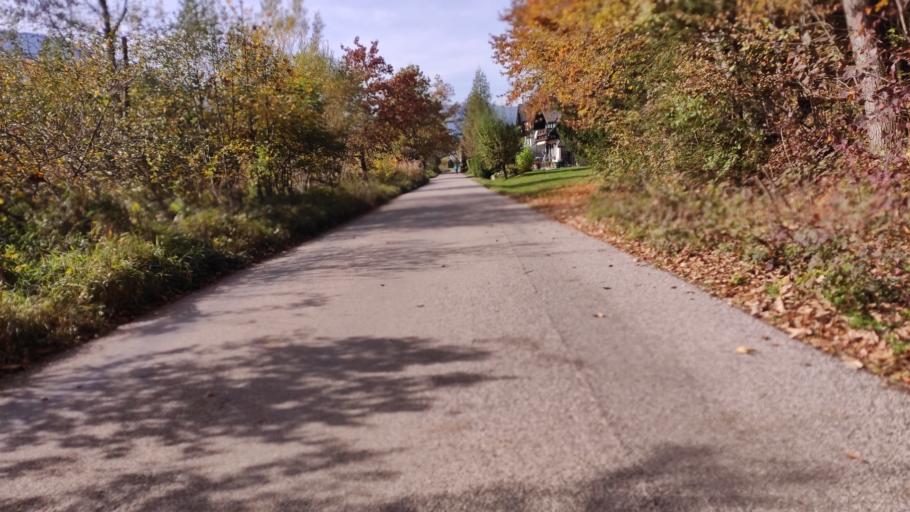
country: AT
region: Salzburg
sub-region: Politischer Bezirk Salzburg-Umgebung
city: Strobl
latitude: 47.7234
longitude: 13.4953
